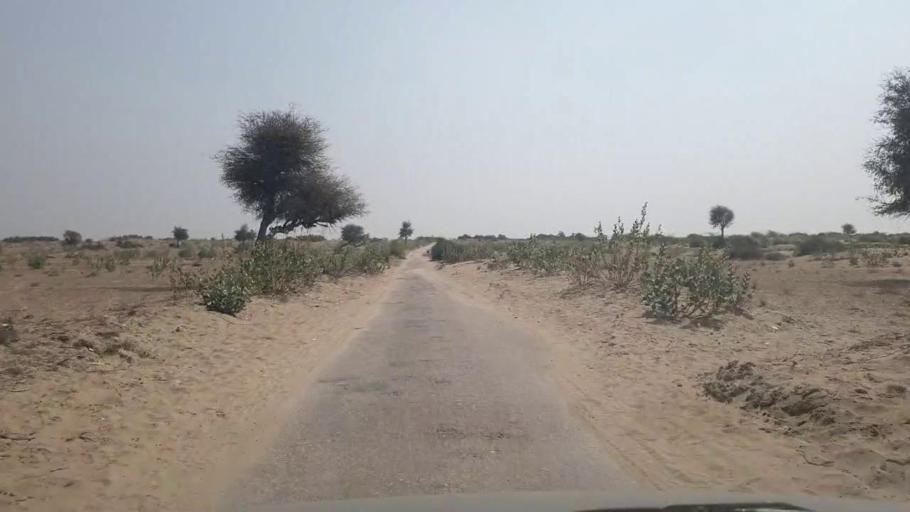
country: PK
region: Sindh
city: Chor
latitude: 25.4628
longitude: 69.7805
